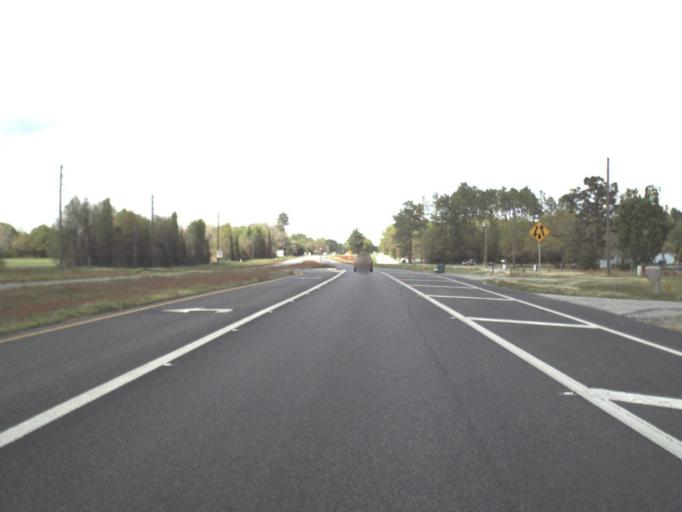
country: US
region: Florida
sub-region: Okaloosa County
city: Crestview
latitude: 30.8250
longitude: -86.5357
